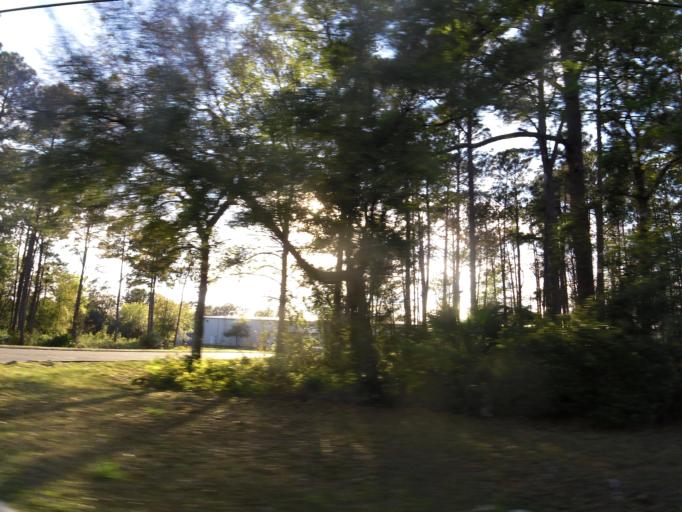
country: US
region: Florida
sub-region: Duval County
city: Jacksonville
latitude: 30.4408
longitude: -81.6052
